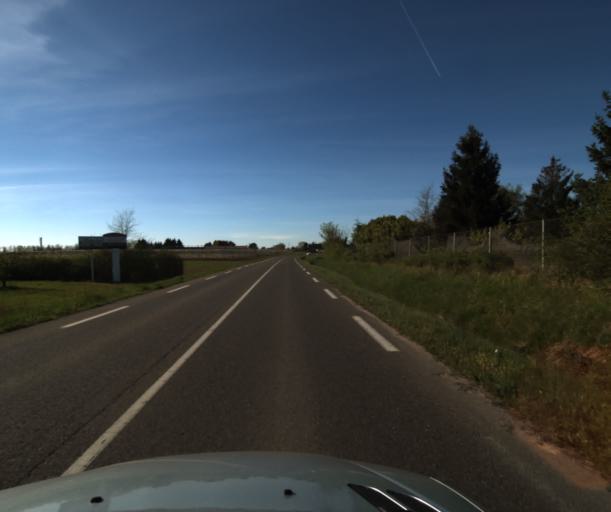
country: FR
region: Midi-Pyrenees
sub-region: Departement du Tarn-et-Garonne
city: Montbeton
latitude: 44.0350
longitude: 1.3123
